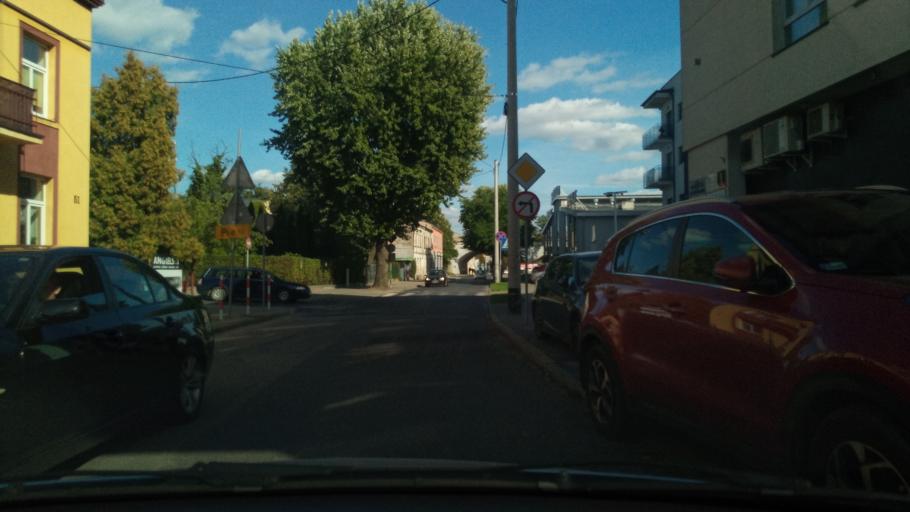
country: PL
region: Lodz Voivodeship
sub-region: Piotrkow Trybunalski
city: Piotrkow Trybunalski
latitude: 51.4074
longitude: 19.6819
